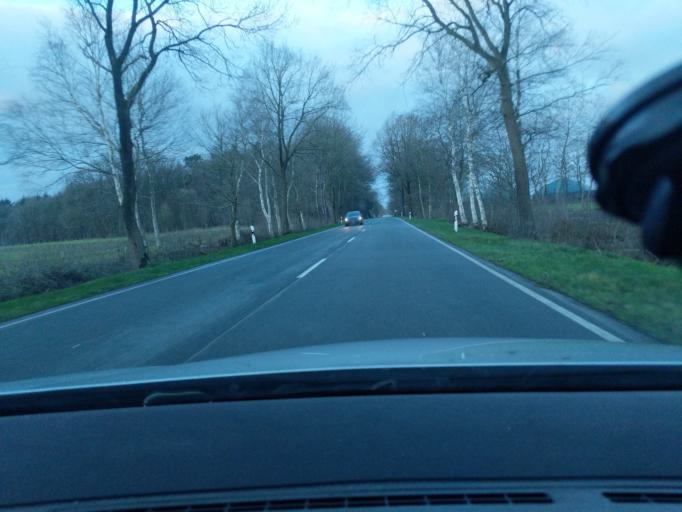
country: DE
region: Lower Saxony
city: Lintig
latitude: 53.6197
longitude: 8.9304
